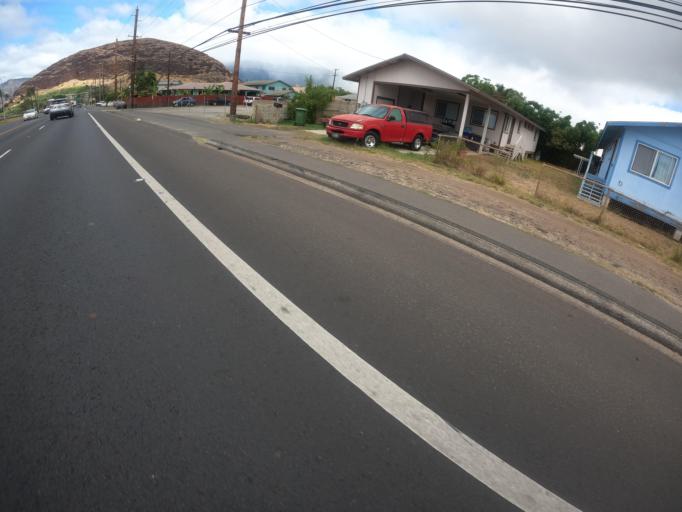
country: US
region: Hawaii
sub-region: Honolulu County
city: Ma'ili
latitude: 21.4219
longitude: -158.1776
